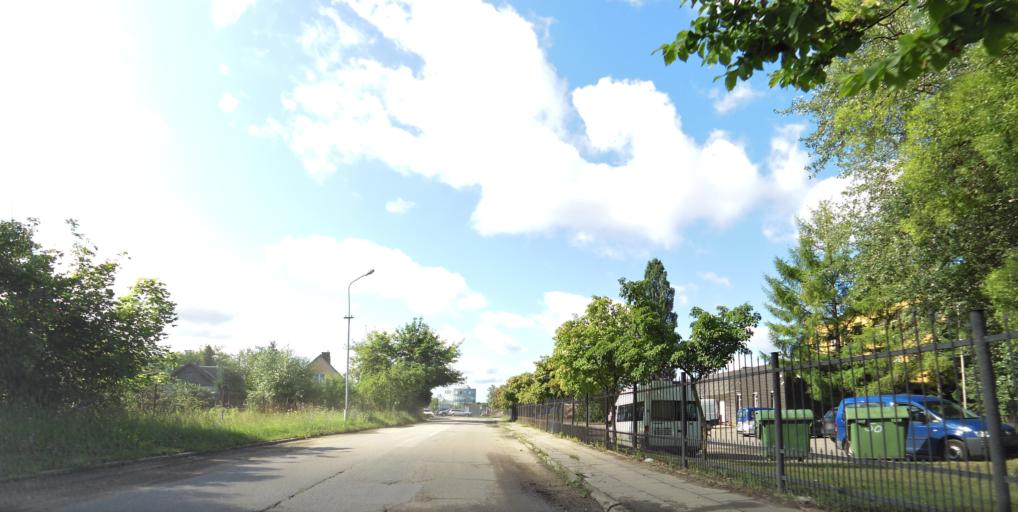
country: LT
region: Vilnius County
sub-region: Vilnius
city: Vilnius
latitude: 54.7068
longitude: 25.2715
